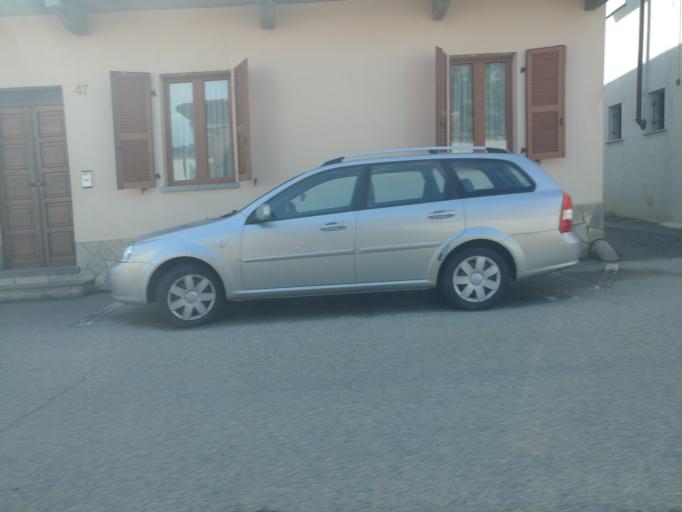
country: IT
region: Piedmont
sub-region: Provincia di Torino
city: Pancalieri
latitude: 44.8323
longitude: 7.5895
